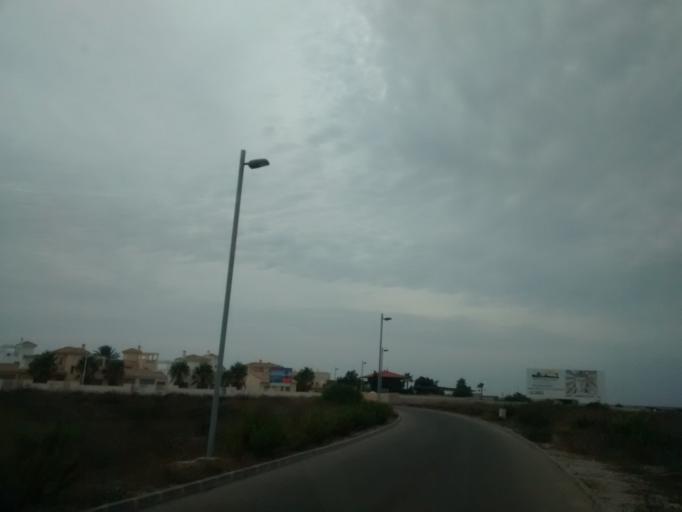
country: ES
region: Murcia
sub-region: Murcia
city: San Pedro del Pinatar
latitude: 37.7787
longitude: -0.7510
